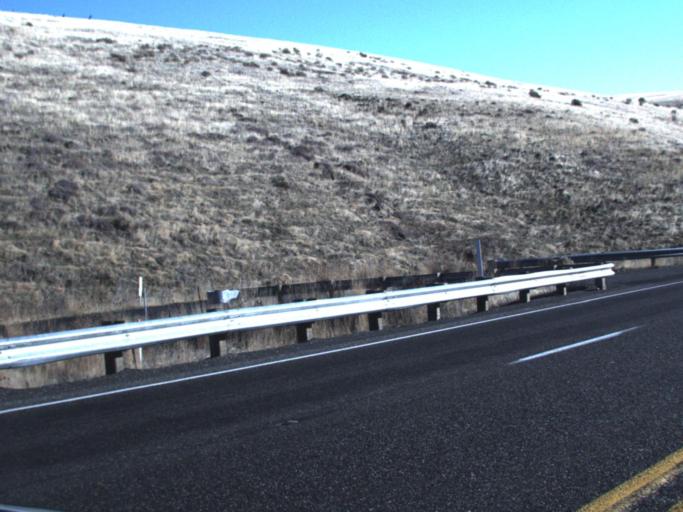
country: US
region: Washington
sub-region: Garfield County
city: Pomeroy
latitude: 46.4441
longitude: -117.4009
